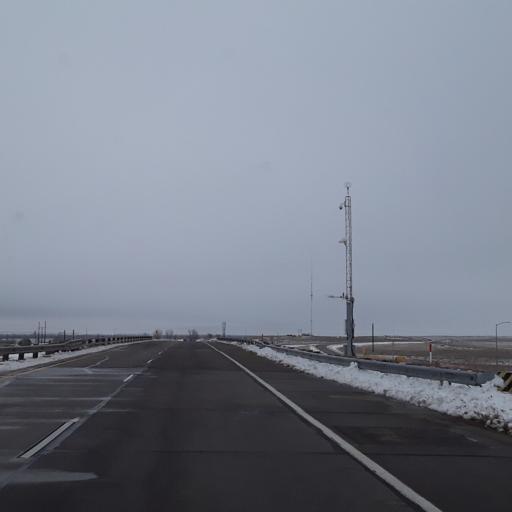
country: US
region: Colorado
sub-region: Logan County
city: Sterling
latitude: 40.6204
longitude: -103.1730
